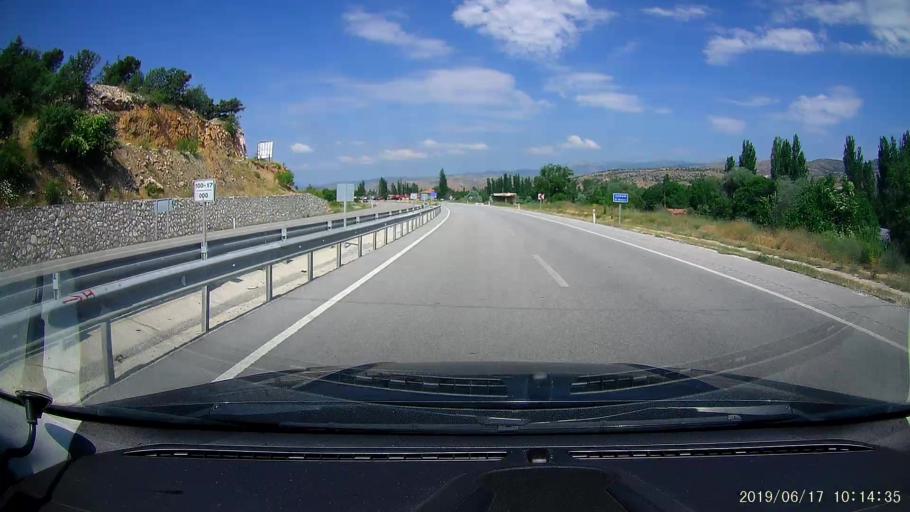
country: TR
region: Amasya
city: Saraycik
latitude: 40.9919
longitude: 35.0234
